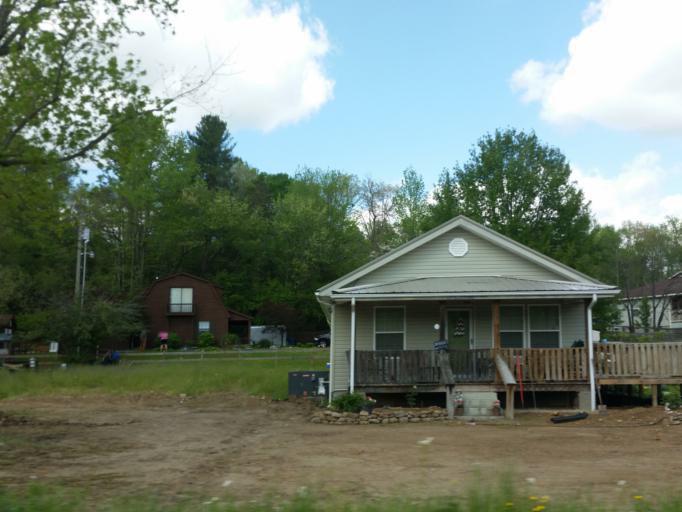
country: US
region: Kentucky
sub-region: Bell County
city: Middlesboro
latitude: 36.6305
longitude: -83.7183
